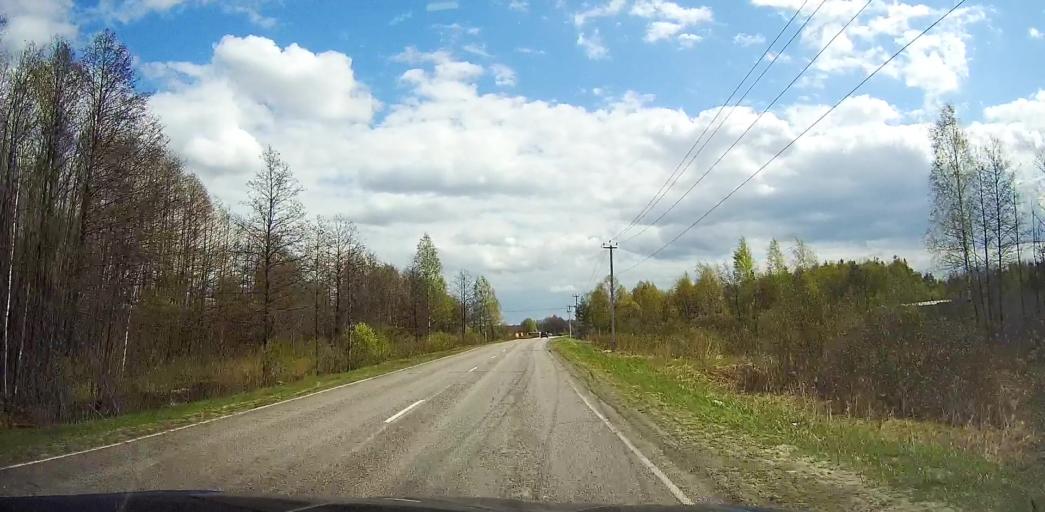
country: RU
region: Moskovskaya
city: Davydovo
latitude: 55.5503
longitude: 38.7998
